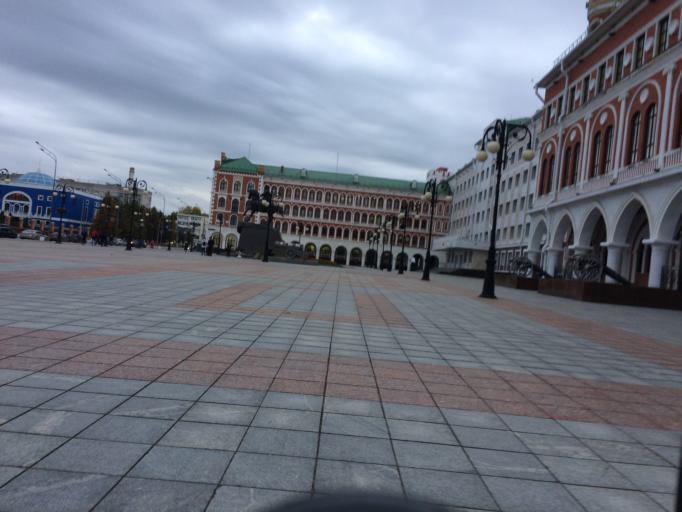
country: RU
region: Mariy-El
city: Yoshkar-Ola
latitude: 56.6316
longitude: 47.8874
